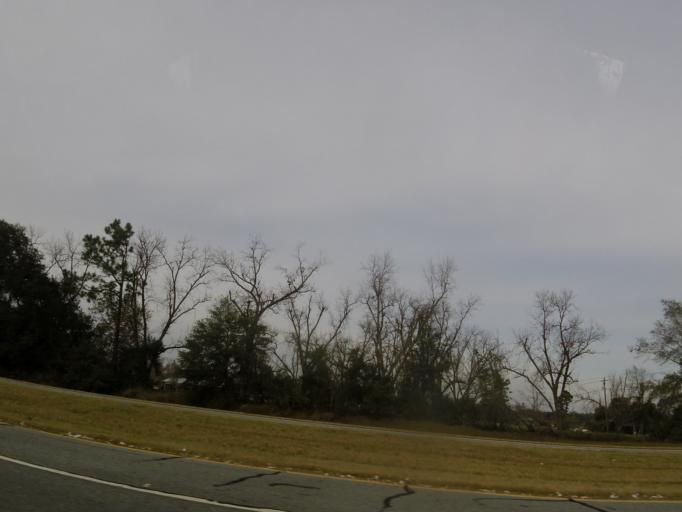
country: US
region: Georgia
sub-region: Seminole County
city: Donalsonville
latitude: 31.0092
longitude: -84.8074
